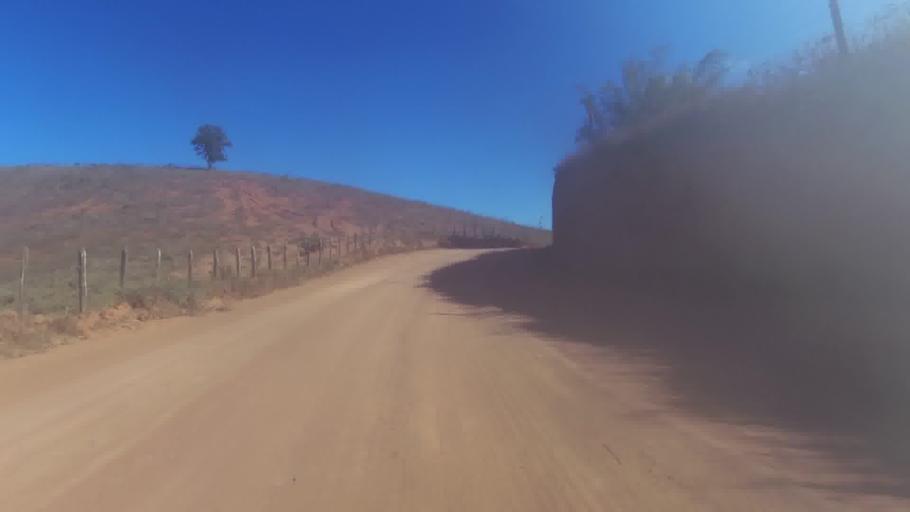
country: BR
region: Espirito Santo
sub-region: Cachoeiro De Itapemirim
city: Cachoeiro de Itapemirim
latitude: -21.0269
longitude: -41.0549
